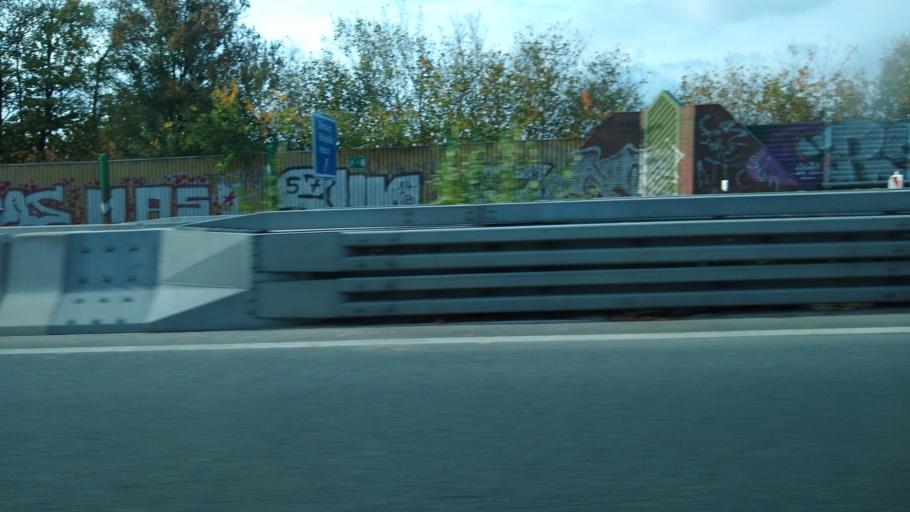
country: DE
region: Lower Saxony
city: Oldenburg
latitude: 53.1733
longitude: 8.2243
